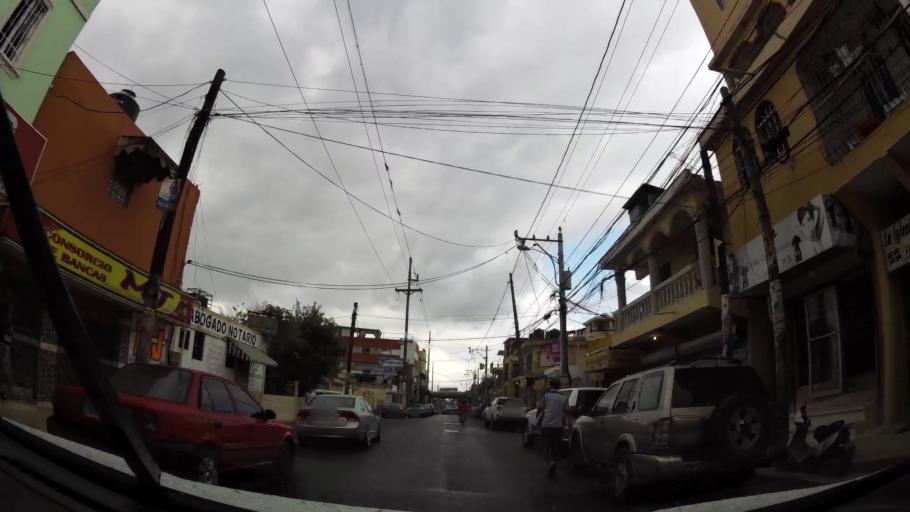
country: DO
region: Nacional
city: La Agustina
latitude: 18.5016
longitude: -69.9171
